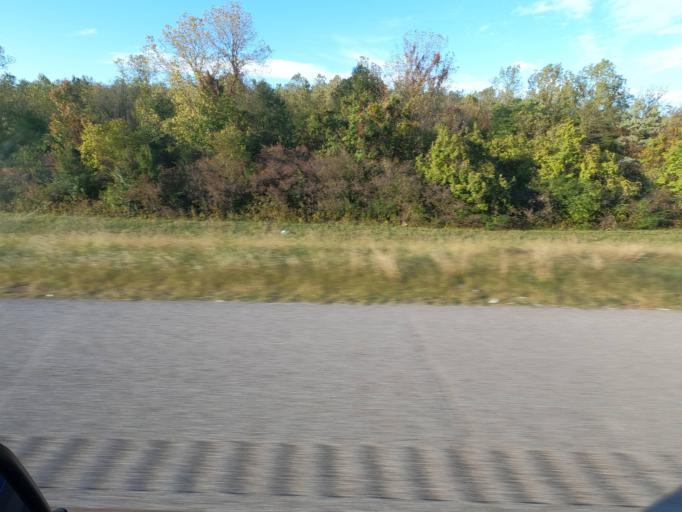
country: US
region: Tennessee
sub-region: Shelby County
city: Millington
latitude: 35.3306
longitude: -89.9083
